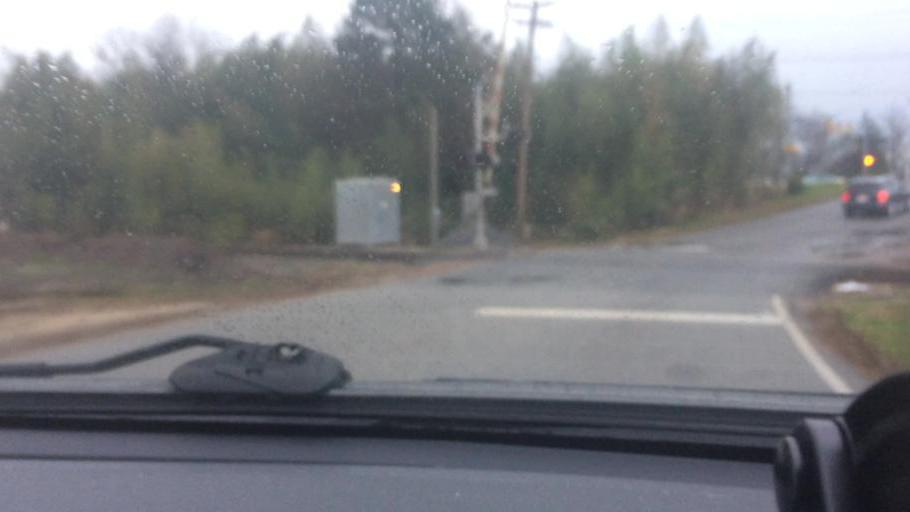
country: US
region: South Carolina
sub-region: Greenville County
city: Wade Hampton
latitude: 34.8953
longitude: -82.3698
